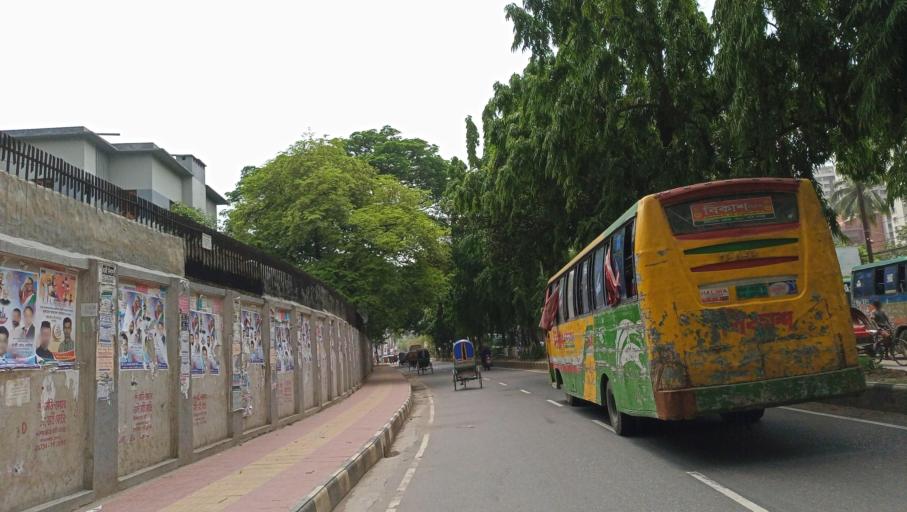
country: BD
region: Dhaka
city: Azimpur
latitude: 23.7285
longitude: 90.3861
